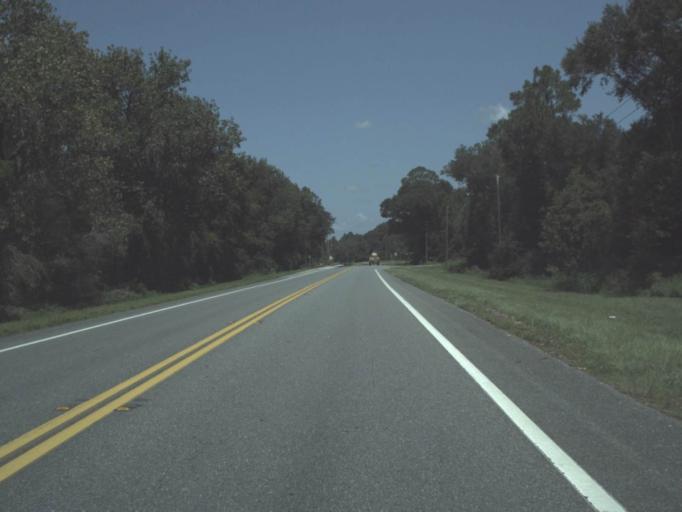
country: US
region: Florida
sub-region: Taylor County
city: Perry
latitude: 30.0862
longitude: -83.5285
